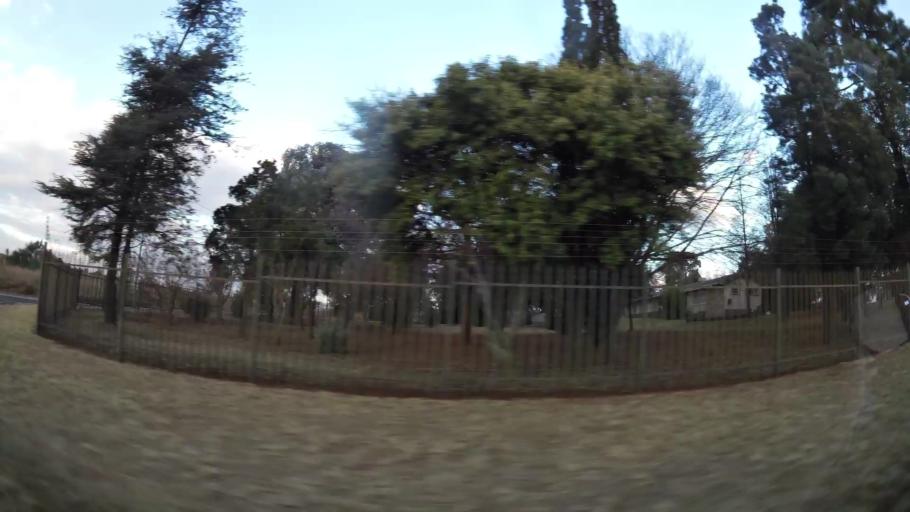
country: ZA
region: Gauteng
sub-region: West Rand District Municipality
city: Krugersdorp
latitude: -26.0723
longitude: 27.7897
